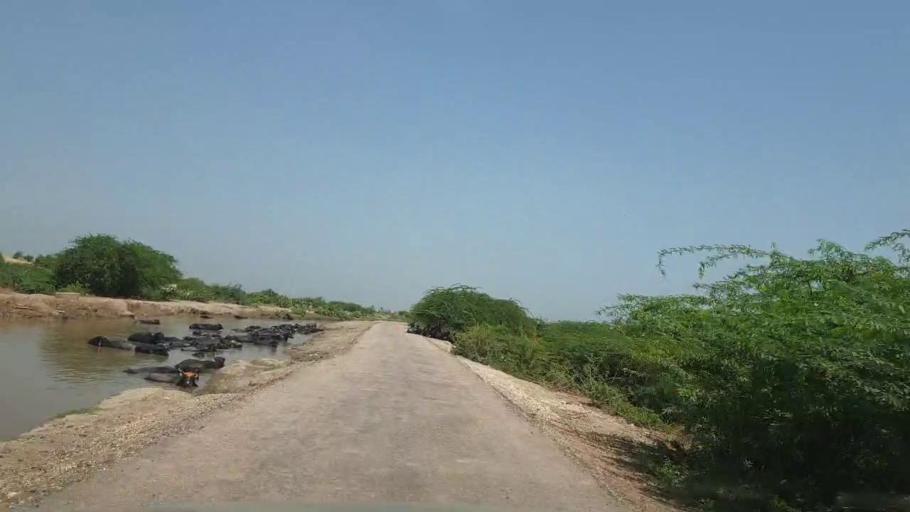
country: PK
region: Sindh
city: Rohri
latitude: 27.6215
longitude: 69.0980
